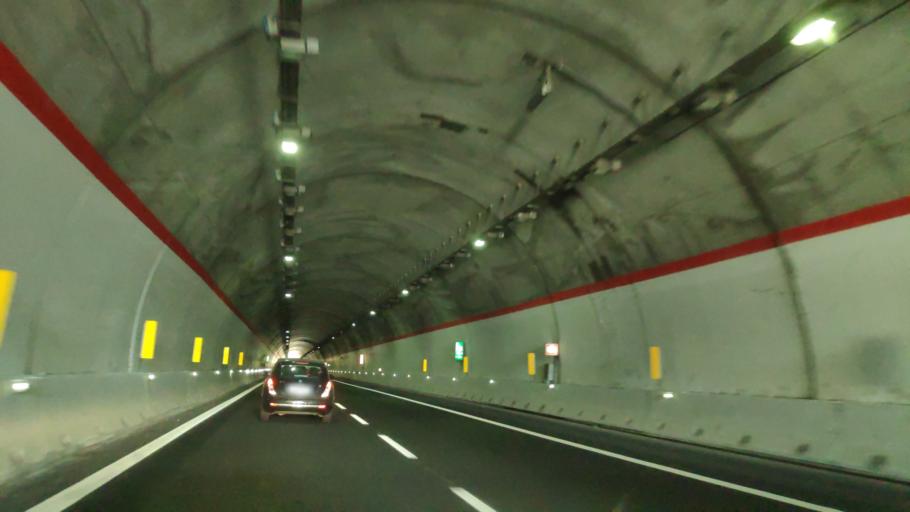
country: IT
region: Basilicate
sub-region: Provincia di Potenza
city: Lagonegro
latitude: 40.1617
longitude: 15.7341
